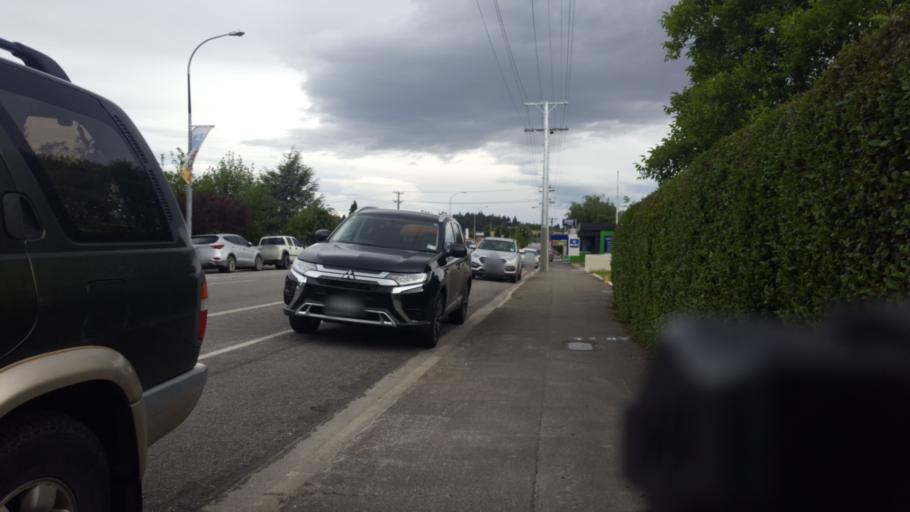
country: NZ
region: Otago
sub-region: Queenstown-Lakes District
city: Wanaka
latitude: -45.2542
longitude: 169.3941
